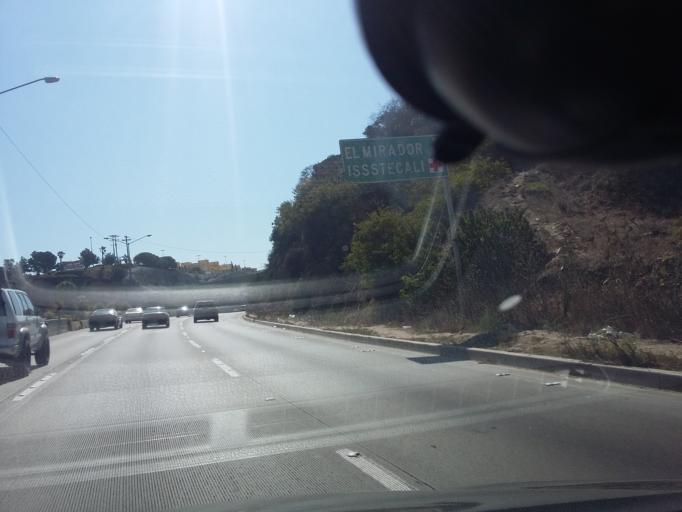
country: US
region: California
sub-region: San Diego County
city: Imperial Beach
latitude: 32.5364
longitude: -117.0929
